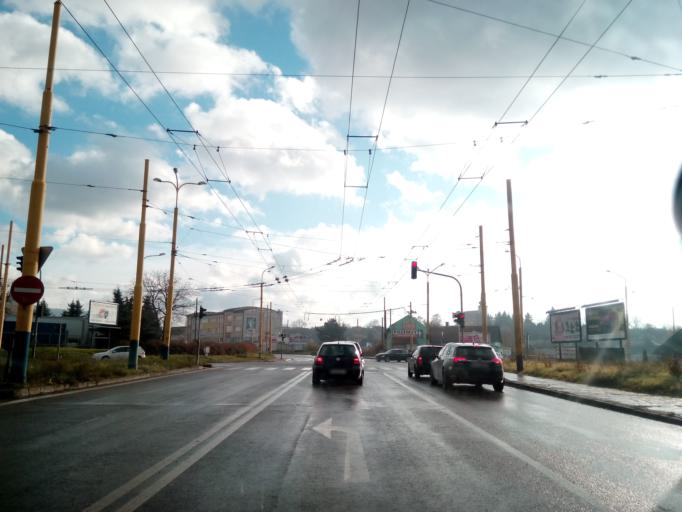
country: SK
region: Presovsky
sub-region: Okres Presov
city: Presov
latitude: 48.9779
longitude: 21.2633
